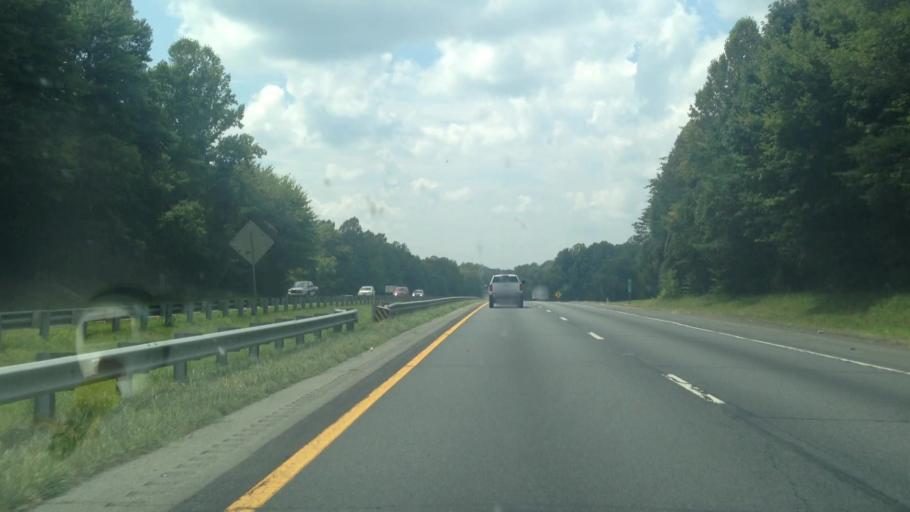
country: US
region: North Carolina
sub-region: Forsyth County
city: Rural Hall
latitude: 36.2287
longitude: -80.3239
